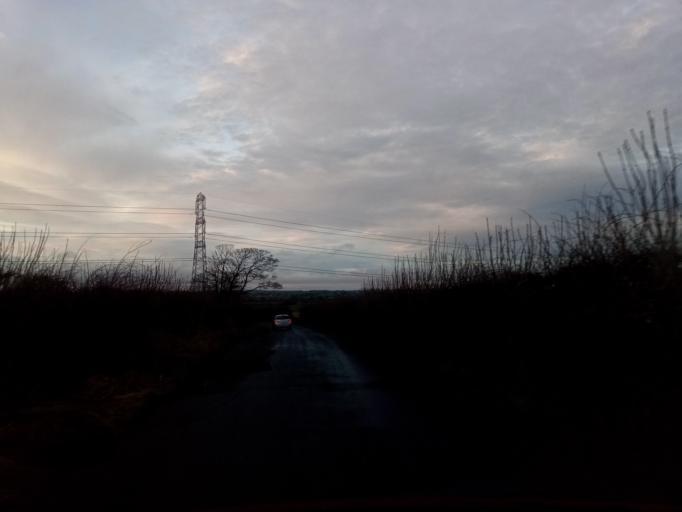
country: GB
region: England
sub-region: Northumberland
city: Ponteland
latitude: 55.0775
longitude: -1.7361
